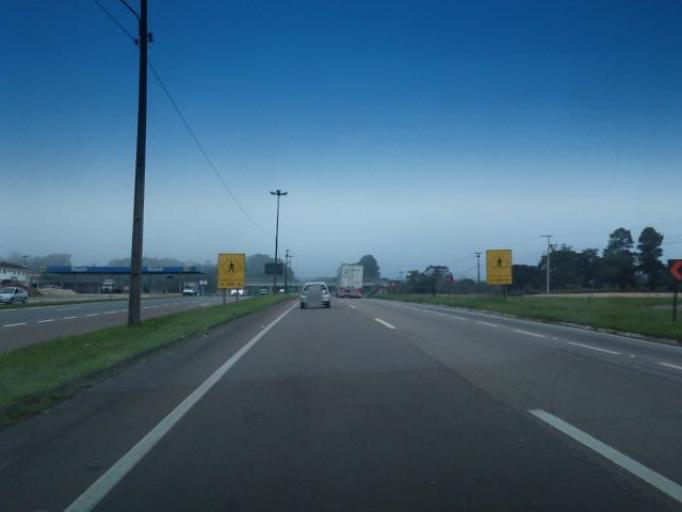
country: BR
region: Parana
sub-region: Sao Jose Dos Pinhais
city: Sao Jose dos Pinhais
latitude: -25.8237
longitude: -49.1249
